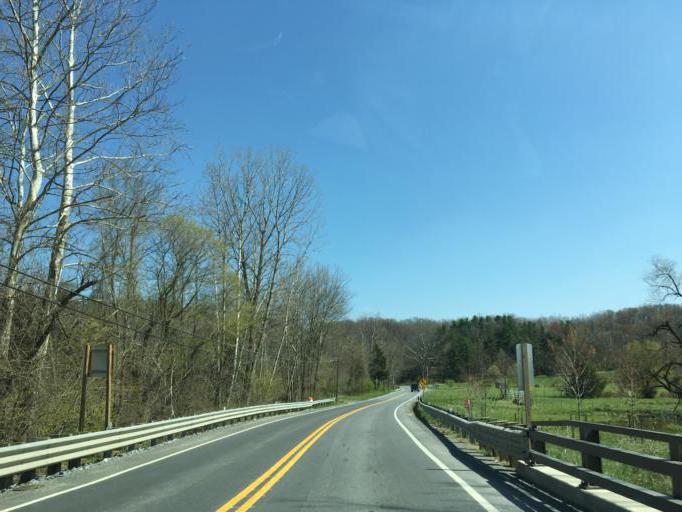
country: US
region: Maryland
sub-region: Frederick County
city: Woodsboro
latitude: 39.5305
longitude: -77.3077
